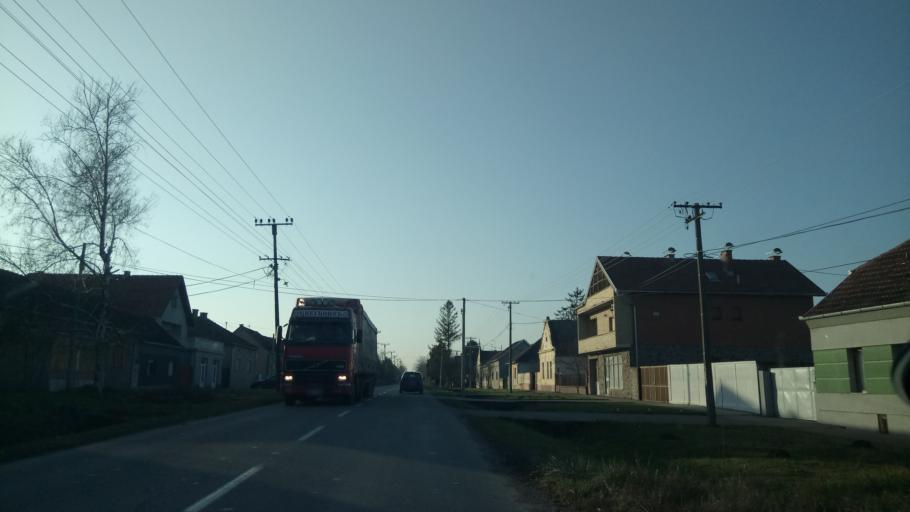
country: RS
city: Beska
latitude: 45.1298
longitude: 20.0747
